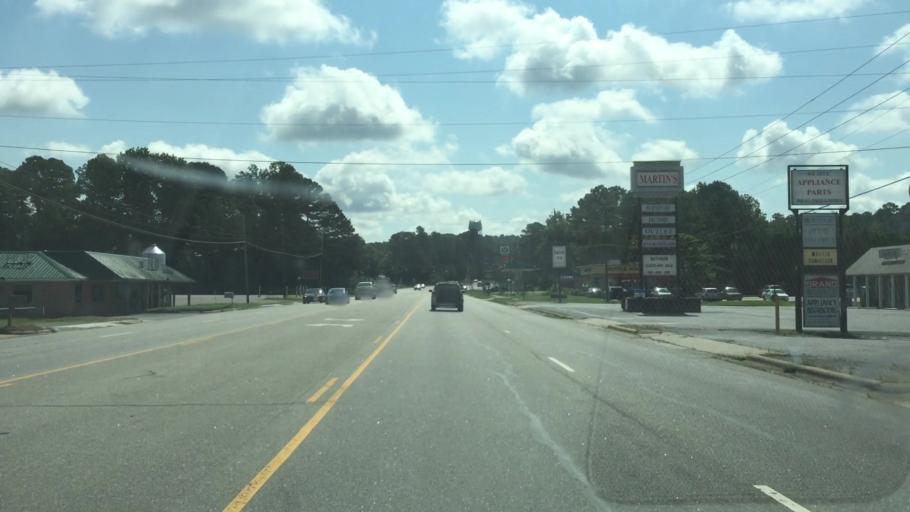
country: US
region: North Carolina
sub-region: Anson County
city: Wadesboro
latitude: 34.9784
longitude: -80.0940
